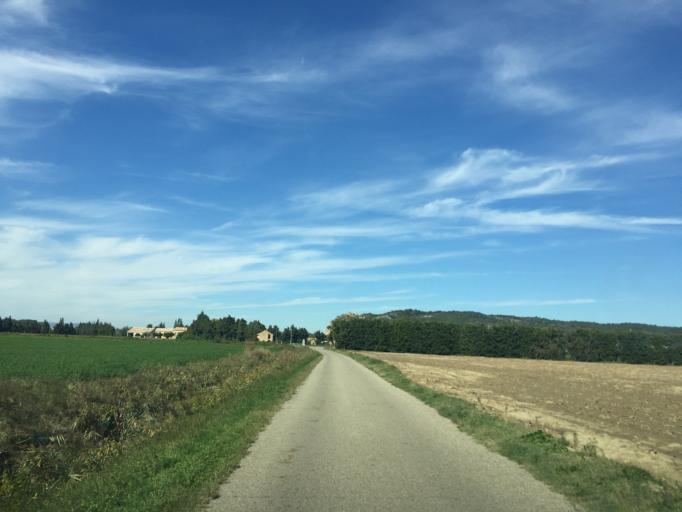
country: FR
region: Provence-Alpes-Cote d'Azur
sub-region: Departement du Vaucluse
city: Mornas
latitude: 44.1863
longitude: 4.7337
